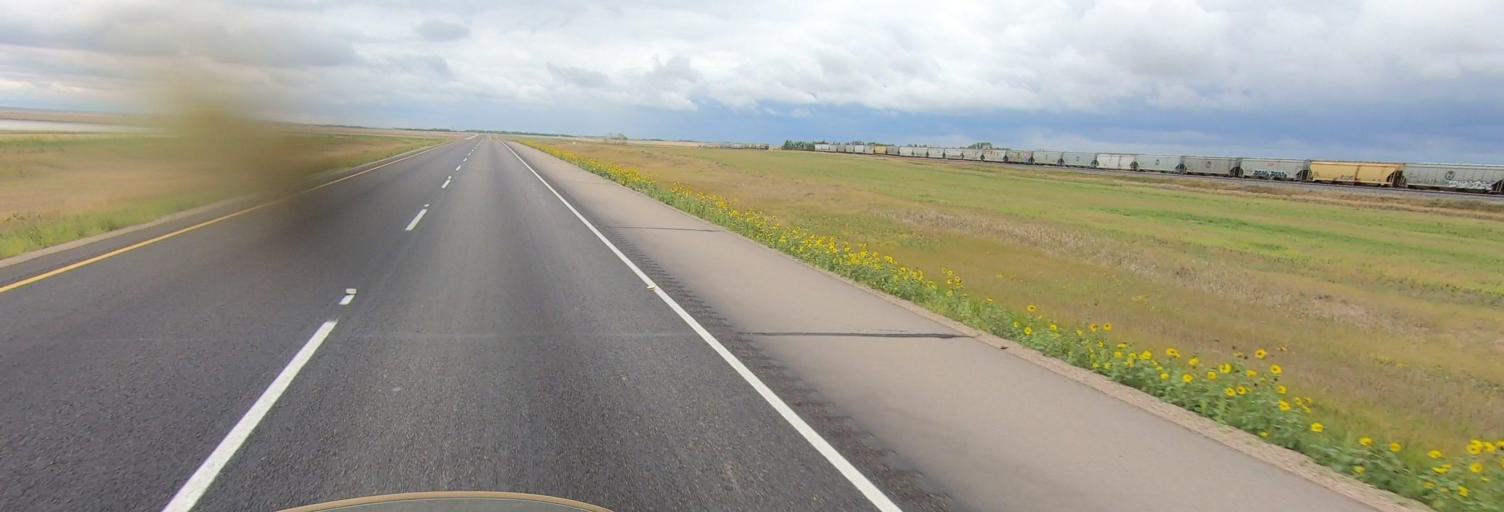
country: CA
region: Saskatchewan
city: Swift Current
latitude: 50.4261
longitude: -107.1405
